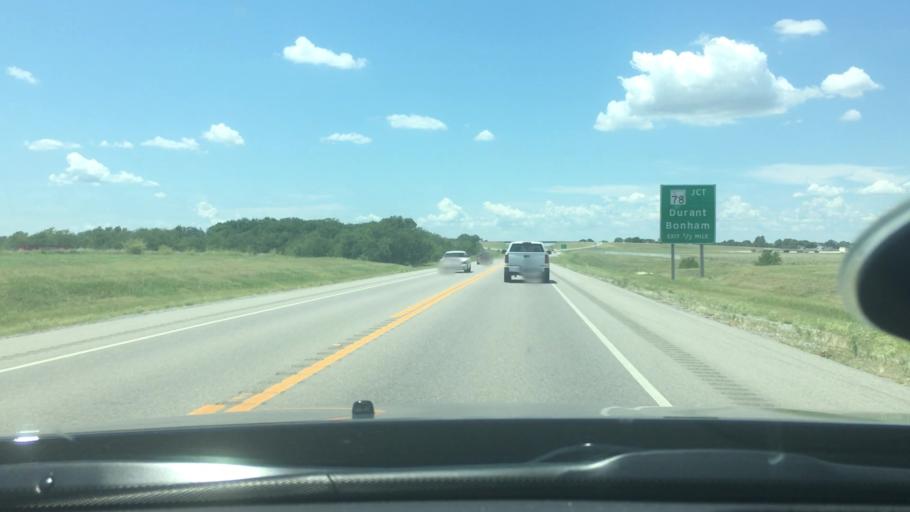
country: US
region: Oklahoma
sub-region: Bryan County
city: Durant
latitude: 33.9653
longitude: -96.3574
